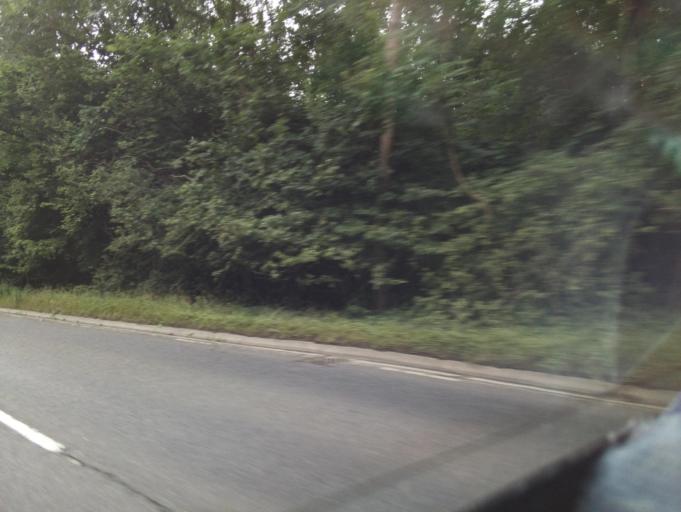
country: GB
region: England
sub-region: Northamptonshire
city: Geddington
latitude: 52.4546
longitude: -0.7365
